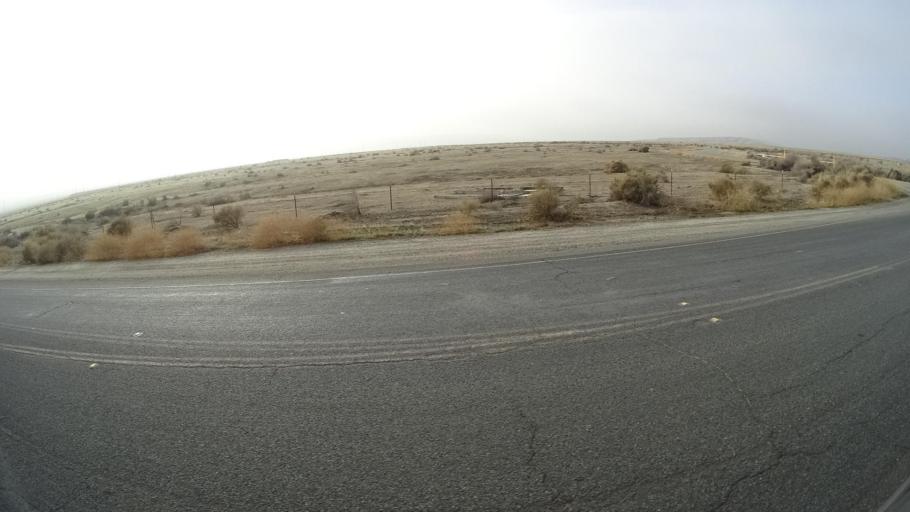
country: US
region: California
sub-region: Kern County
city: Ford City
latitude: 35.2349
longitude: -119.4458
